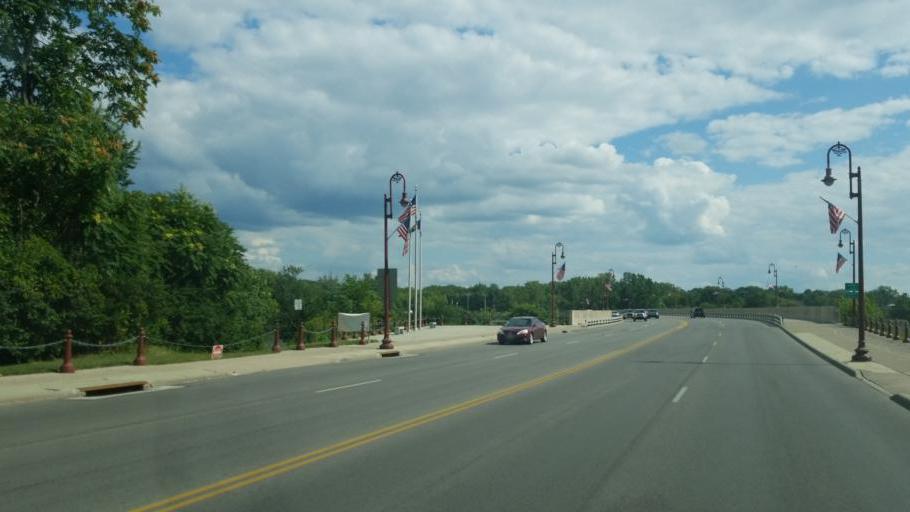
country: US
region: Ohio
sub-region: Lucas County
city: Maumee
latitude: 41.5588
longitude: -83.6518
